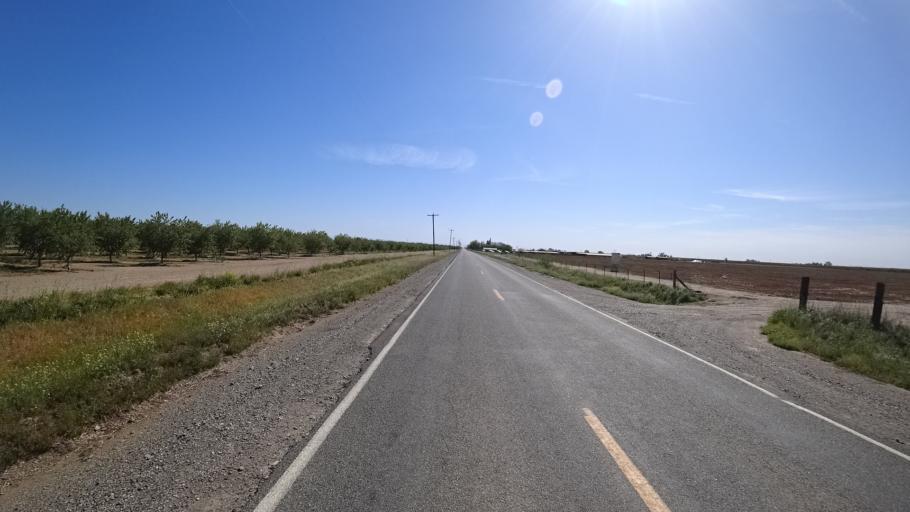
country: US
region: California
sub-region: Glenn County
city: Willows
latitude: 39.6241
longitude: -122.1854
